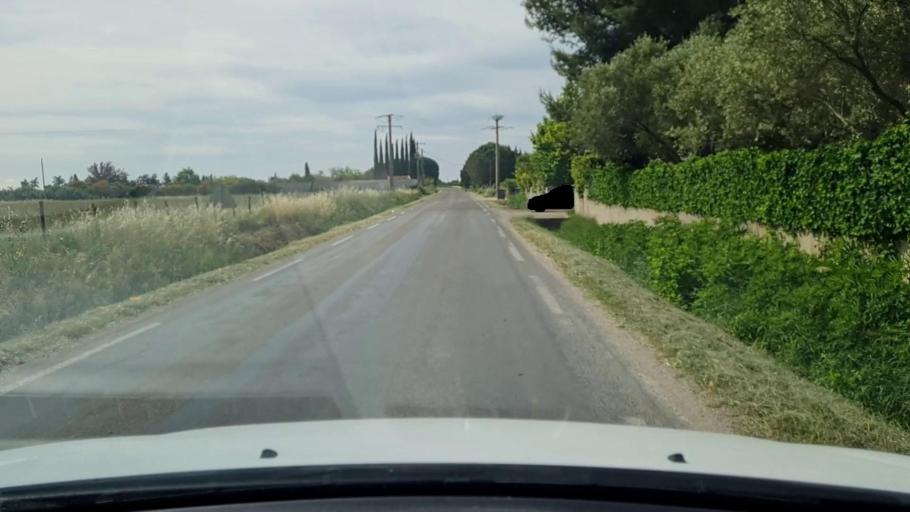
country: FR
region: Languedoc-Roussillon
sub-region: Departement de l'Herault
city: Marsillargues
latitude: 43.6280
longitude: 4.1976
